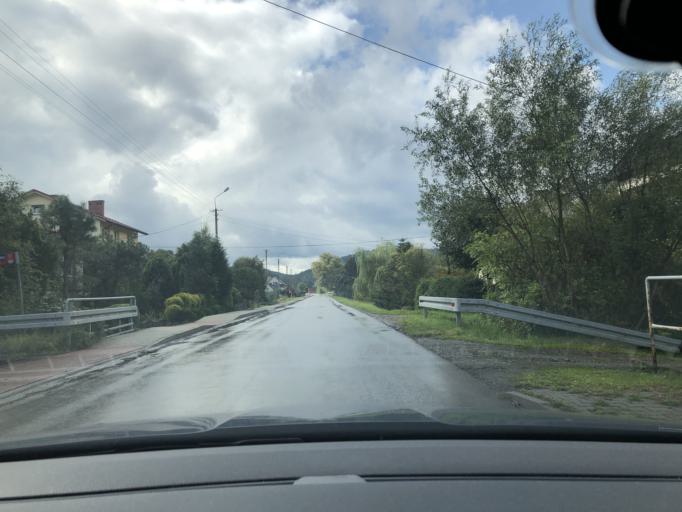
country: PL
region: Lesser Poland Voivodeship
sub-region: Powiat suski
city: Kukow
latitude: 49.7183
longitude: 19.4906
